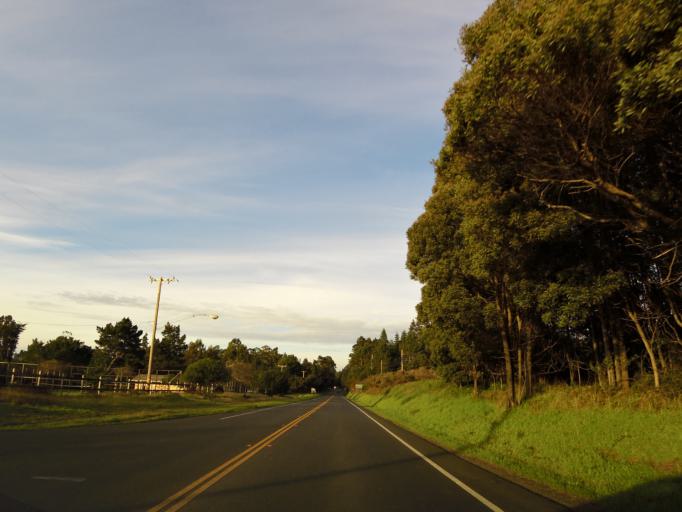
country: US
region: California
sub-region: Mendocino County
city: Fort Bragg
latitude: 39.3884
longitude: -123.8122
